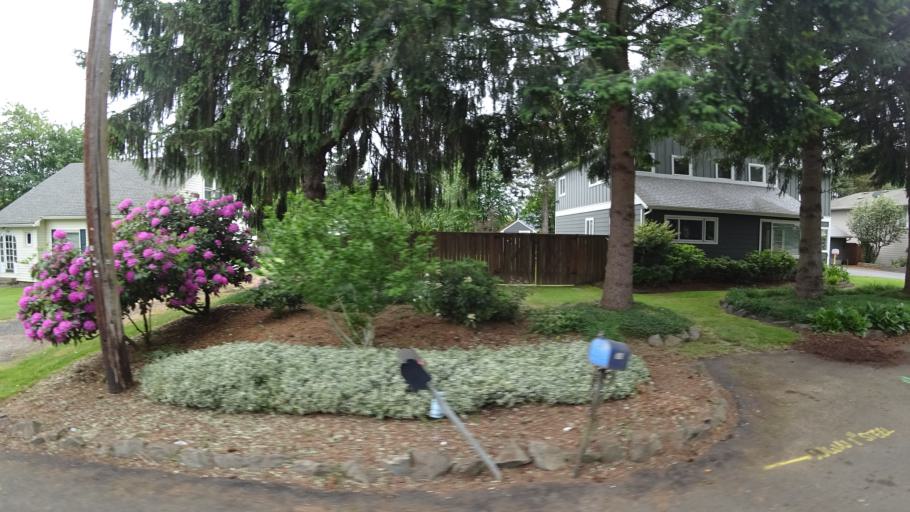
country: US
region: Oregon
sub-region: Washington County
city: Garden Home-Whitford
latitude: 45.4667
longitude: -122.7566
